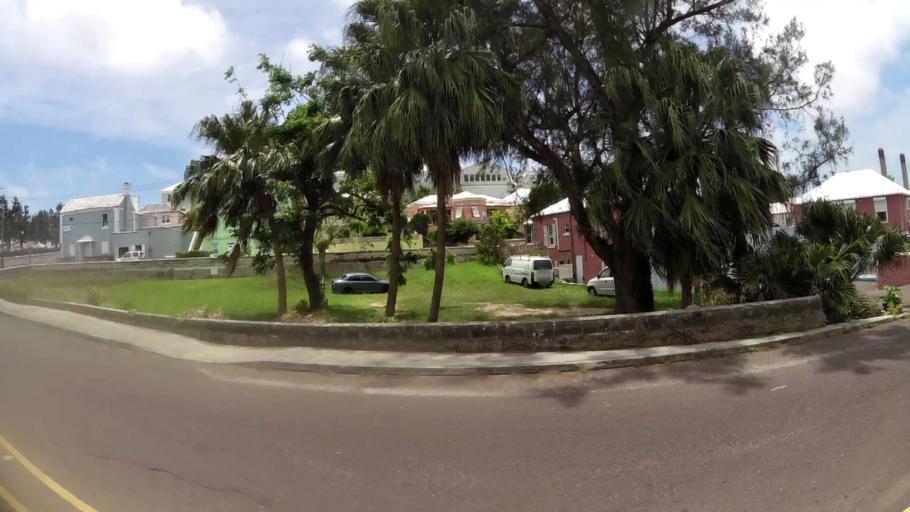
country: BM
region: Hamilton city
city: Hamilton
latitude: 32.3006
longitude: -64.7874
